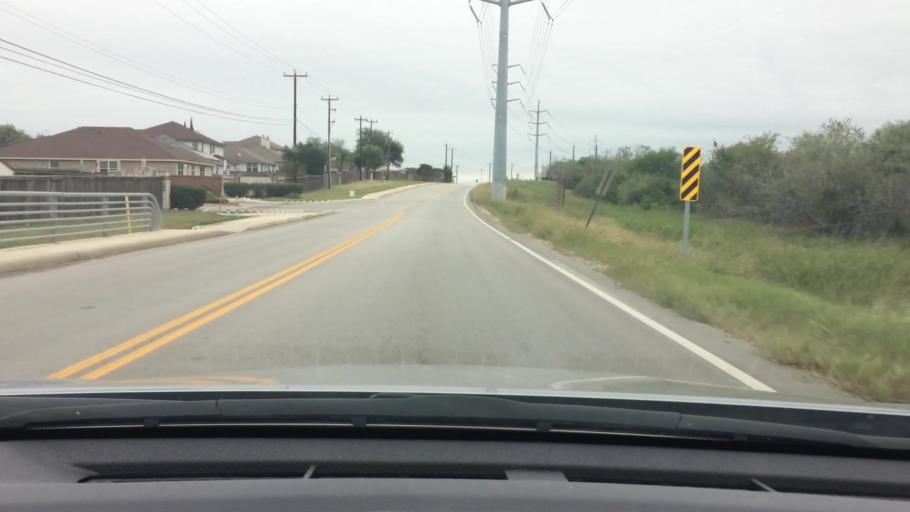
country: US
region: Texas
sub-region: Bexar County
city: Kirby
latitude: 29.4668
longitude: -98.3464
